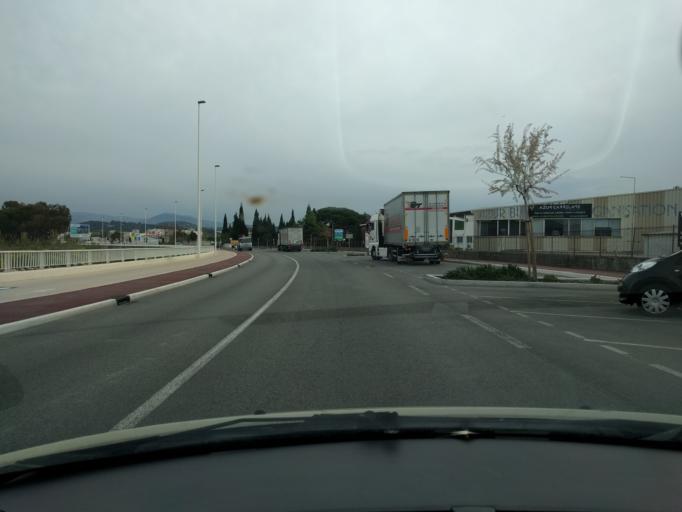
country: FR
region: Provence-Alpes-Cote d'Azur
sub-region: Departement des Alpes-Maritimes
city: Mandelieu-la-Napoule
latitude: 43.5452
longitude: 6.9617
